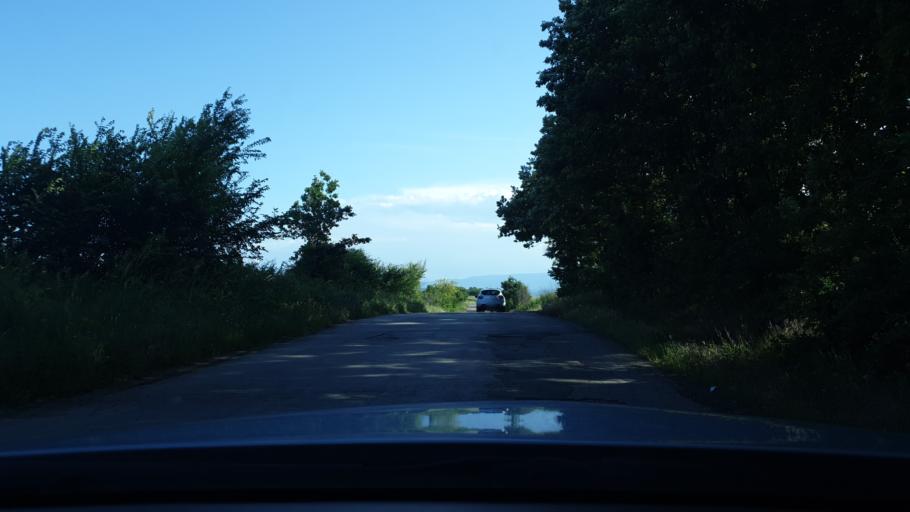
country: RS
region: Central Serbia
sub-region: Nisavski Okrug
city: Aleksinac
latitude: 43.6067
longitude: 21.6473
